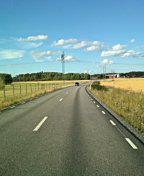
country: SE
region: Uppsala
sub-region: Habo Kommun
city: Balsta
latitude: 59.6386
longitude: 17.5247
